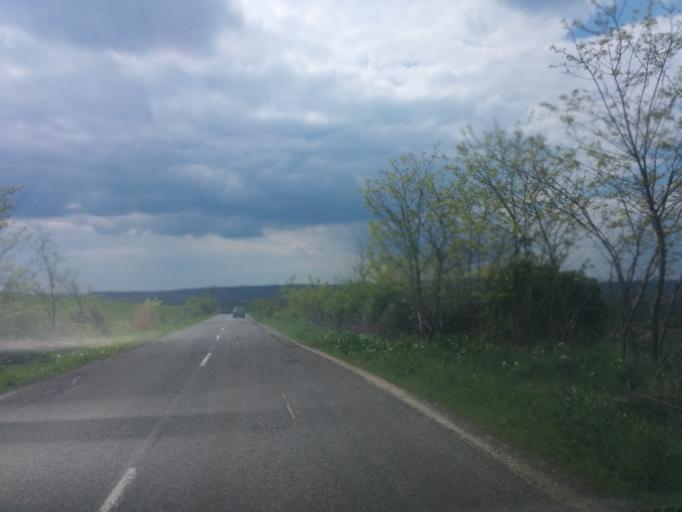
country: HU
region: Nograd
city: Palotas
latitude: 47.8301
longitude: 19.5595
